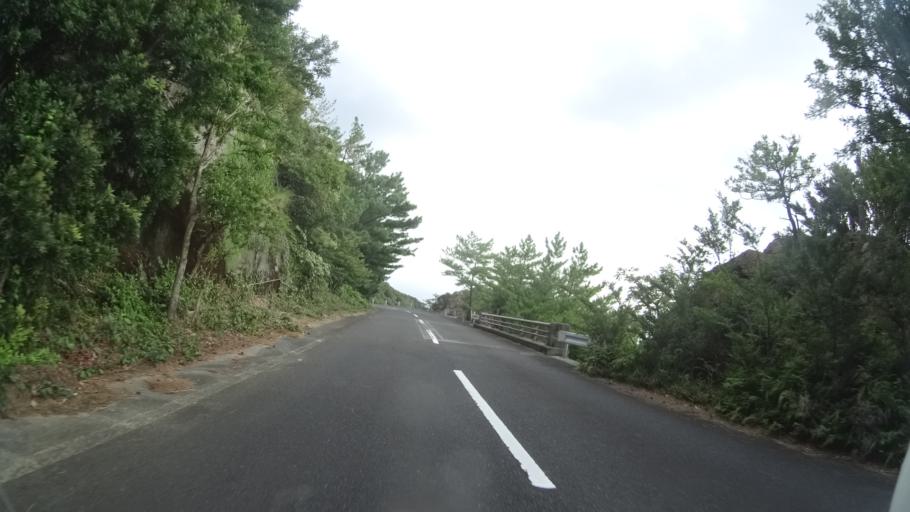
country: JP
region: Kagoshima
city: Nishinoomote
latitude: 30.3302
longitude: 130.3924
